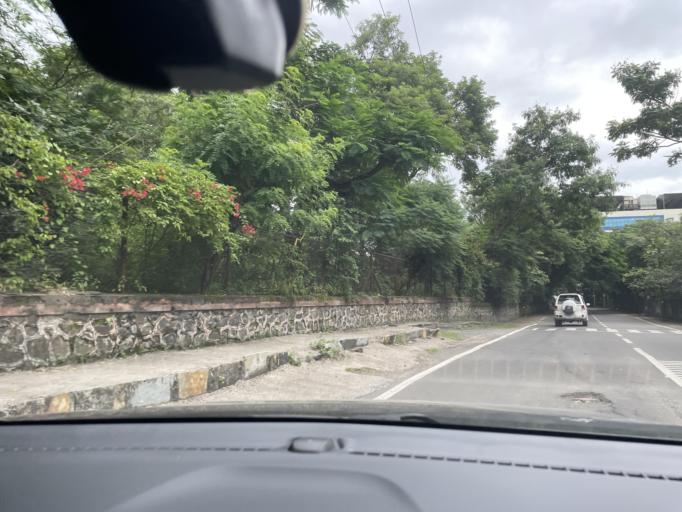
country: IN
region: Maharashtra
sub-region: Pune Division
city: Shivaji Nagar
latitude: 18.5369
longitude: 73.8113
